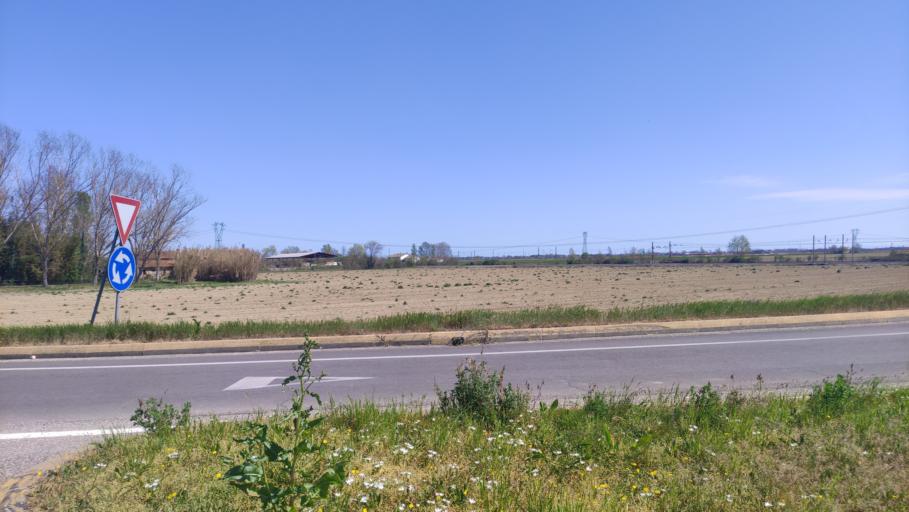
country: IT
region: Emilia-Romagna
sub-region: Provincia di Ravenna
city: Fornace Zarattini
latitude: 44.4070
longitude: 12.1153
